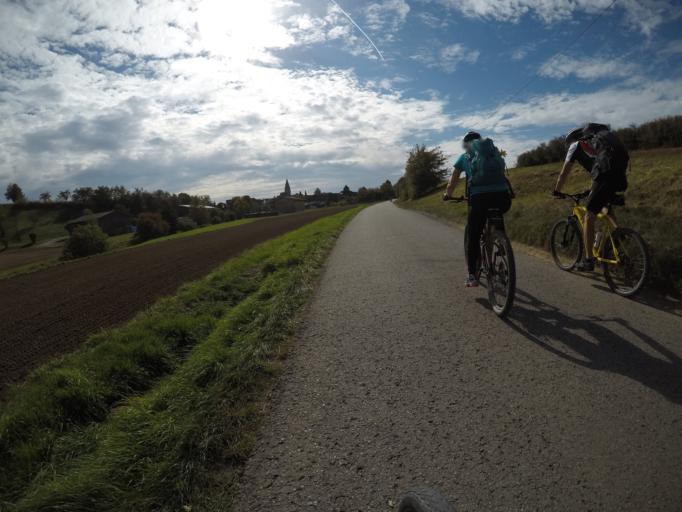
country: DE
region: Baden-Wuerttemberg
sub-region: Regierungsbezirk Stuttgart
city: Hildrizhausen
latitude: 48.6298
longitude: 8.9675
